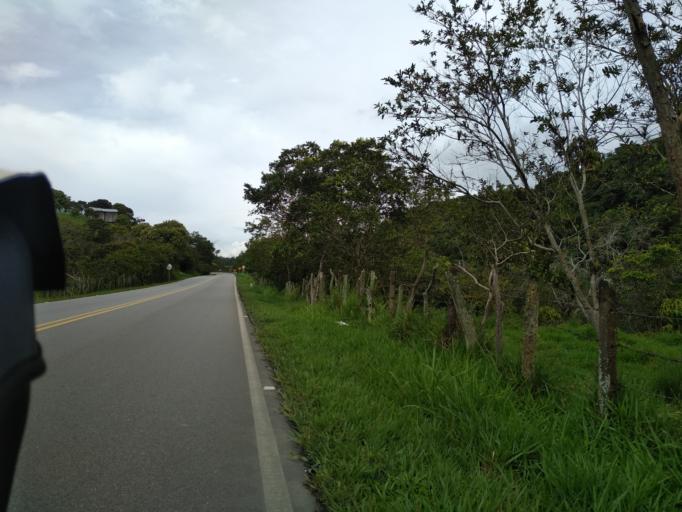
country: CO
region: Santander
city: Suaita
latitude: 6.1063
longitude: -73.3679
